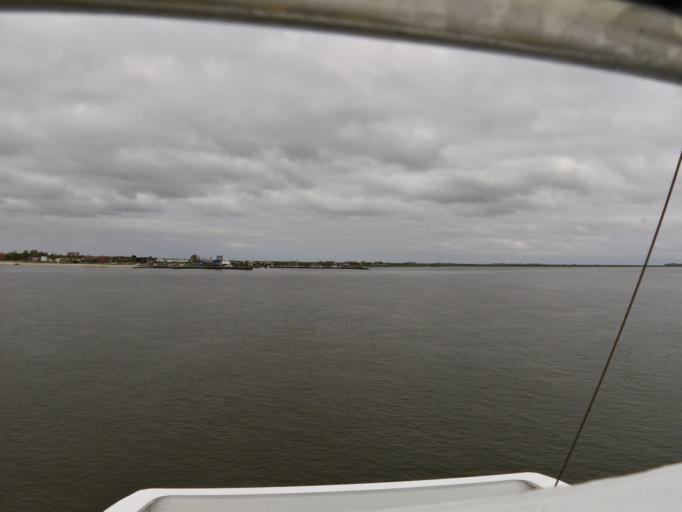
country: DE
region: Schleswig-Holstein
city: Wyk auf Fohr
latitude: 54.6889
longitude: 8.5853
